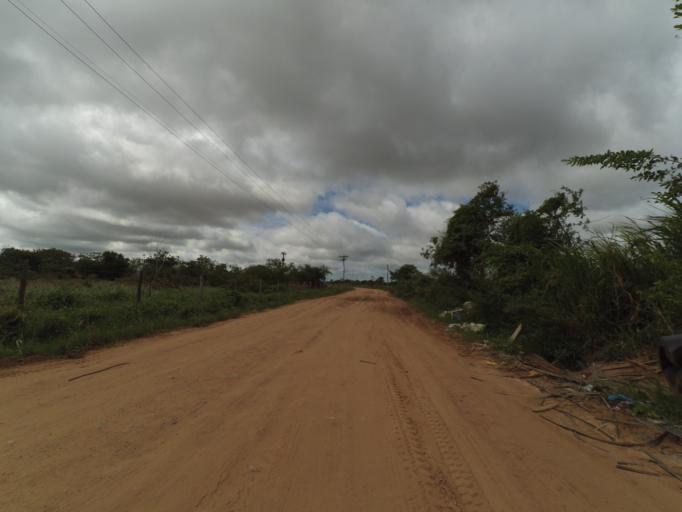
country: BO
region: Santa Cruz
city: Santa Cruz de la Sierra
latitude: -17.8931
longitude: -63.2410
